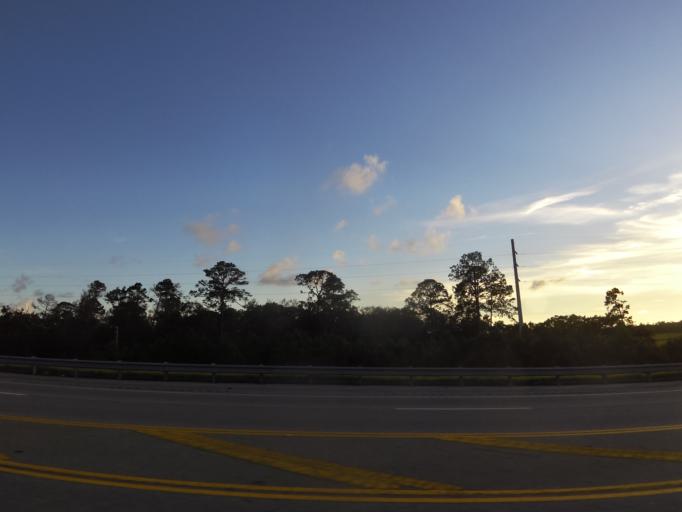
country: US
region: Georgia
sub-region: Glynn County
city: Brunswick
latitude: 31.1218
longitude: -81.5444
